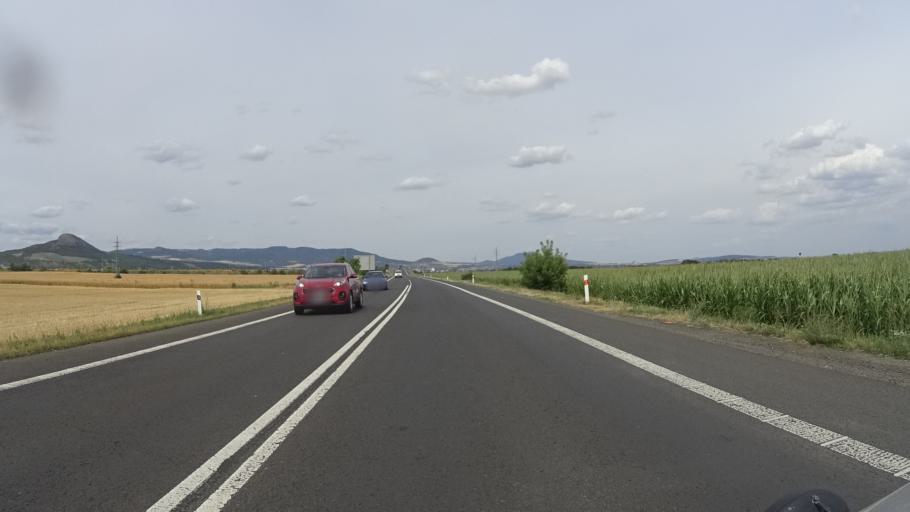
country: CZ
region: Ustecky
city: Lovosice
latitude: 50.4977
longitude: 14.0919
